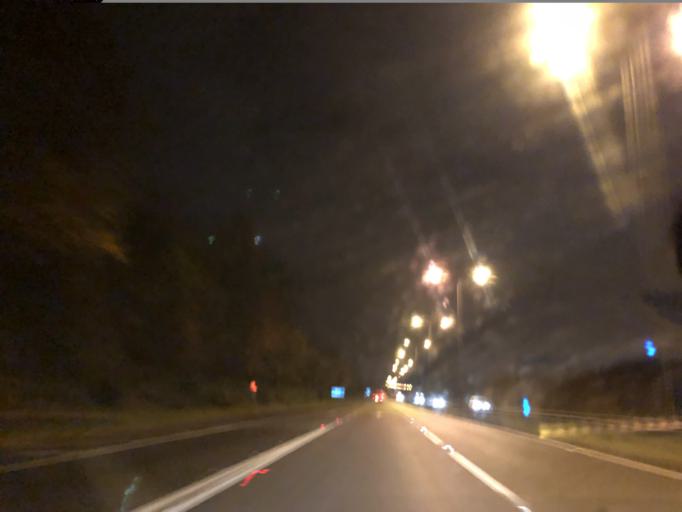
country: GB
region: England
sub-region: Kirklees
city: Cleckheaton
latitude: 53.7438
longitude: -1.7332
